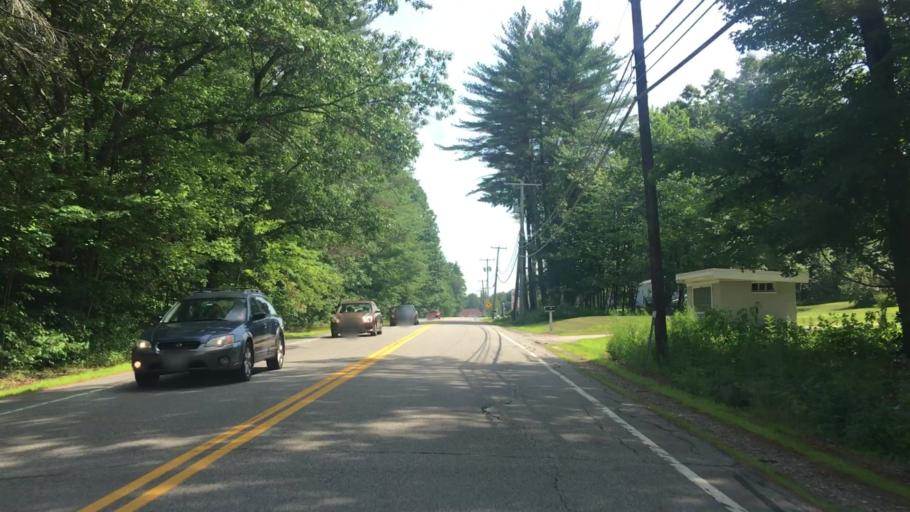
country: US
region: New Hampshire
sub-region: Strafford County
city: Rochester
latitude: 43.3609
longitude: -70.9803
